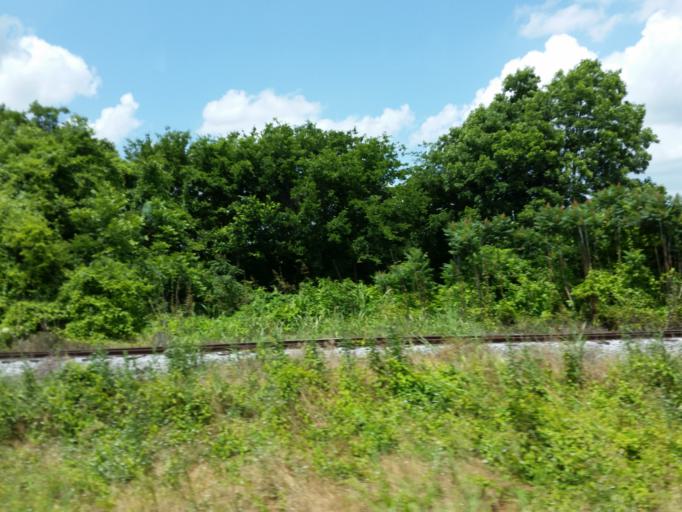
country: US
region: Tennessee
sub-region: Lake County
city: Tiptonville
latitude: 36.3930
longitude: -89.4614
